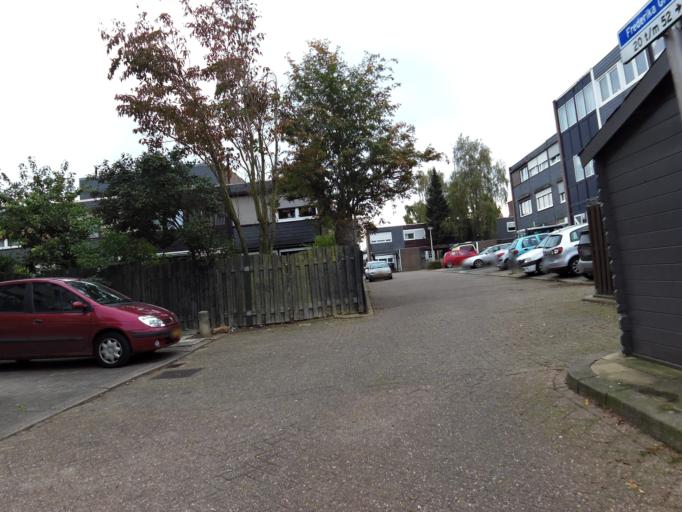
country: NL
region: Limburg
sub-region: Gemeente Simpelveld
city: Simpelveld
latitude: 50.8500
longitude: 6.0191
